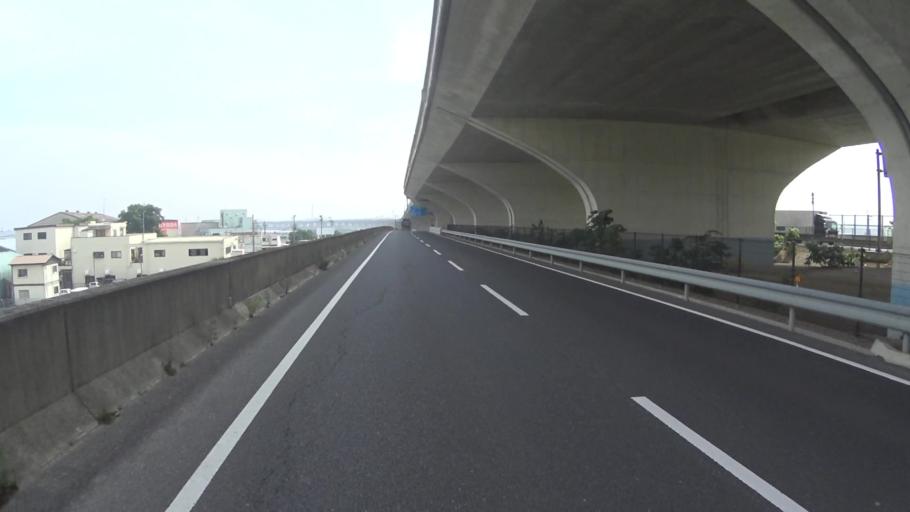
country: JP
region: Kyoto
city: Yawata
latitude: 34.8473
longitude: 135.7267
